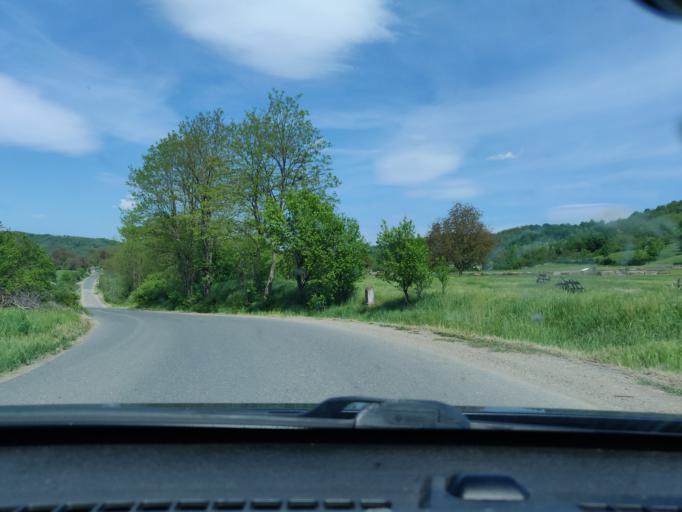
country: RO
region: Vrancea
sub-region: Comuna Vidra
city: Vidra
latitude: 45.9452
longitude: 26.8735
